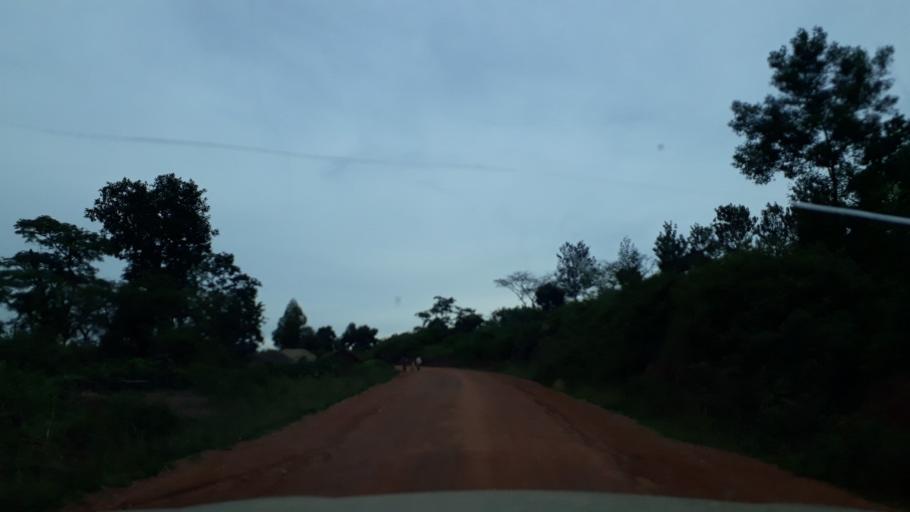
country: UG
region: Northern Region
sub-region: Zombo District
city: Paidha
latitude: 2.2034
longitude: 30.7377
